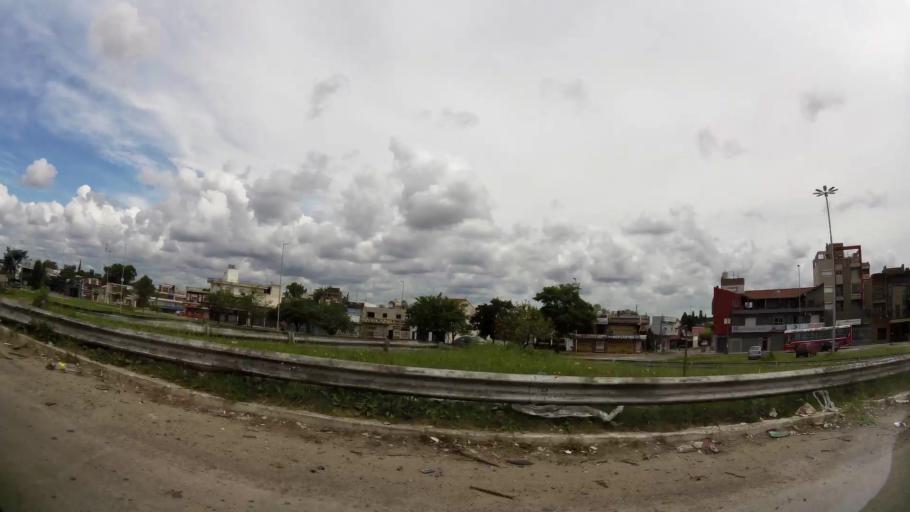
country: AR
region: Buenos Aires
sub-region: Partido de Quilmes
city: Quilmes
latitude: -34.7823
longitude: -58.2610
